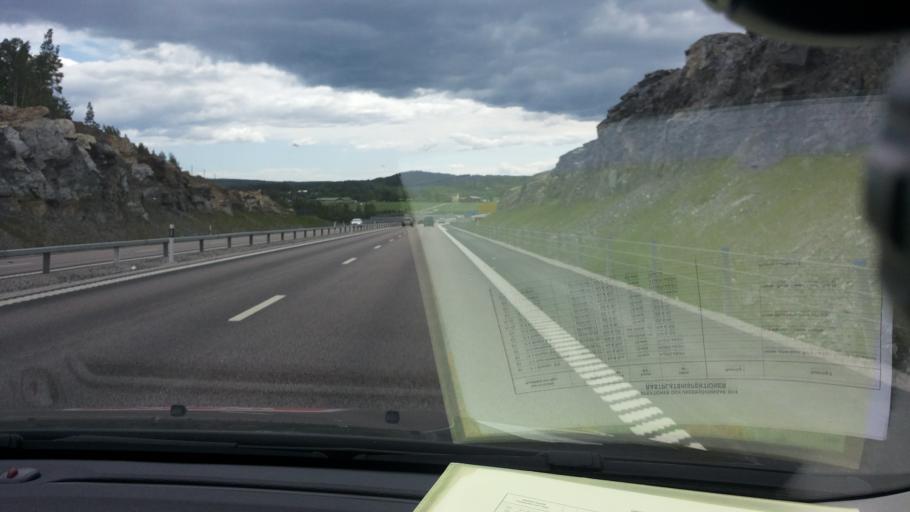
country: SE
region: Vaesternorrland
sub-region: Sundsvalls Kommun
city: Nolby
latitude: 62.3002
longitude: 17.3458
